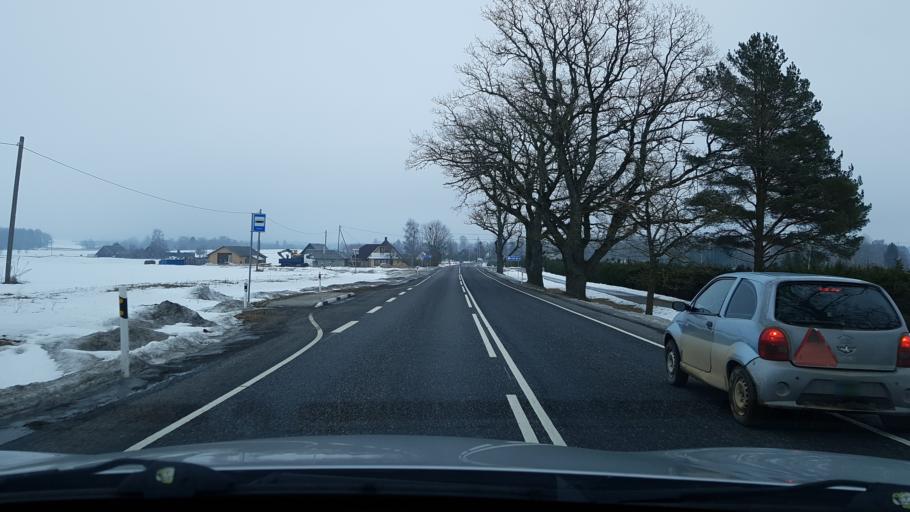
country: EE
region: Vorumaa
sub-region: Antsla vald
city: Vana-Antsla
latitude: 57.9210
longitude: 26.3158
